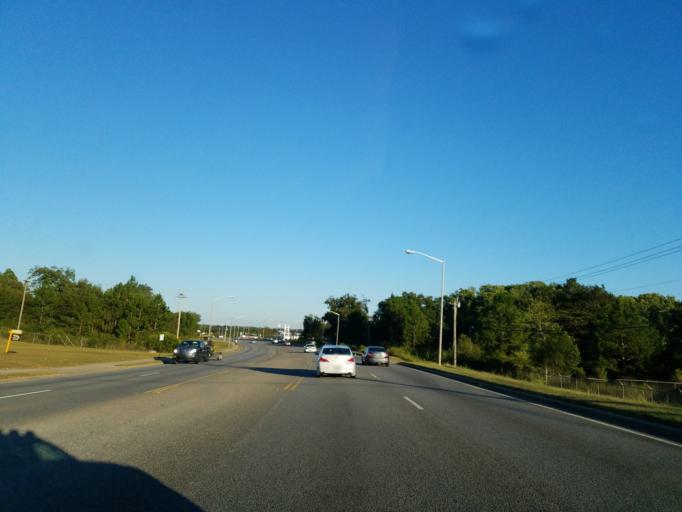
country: US
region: Georgia
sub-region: Worth County
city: Sylvester
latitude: 31.5278
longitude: -83.8197
